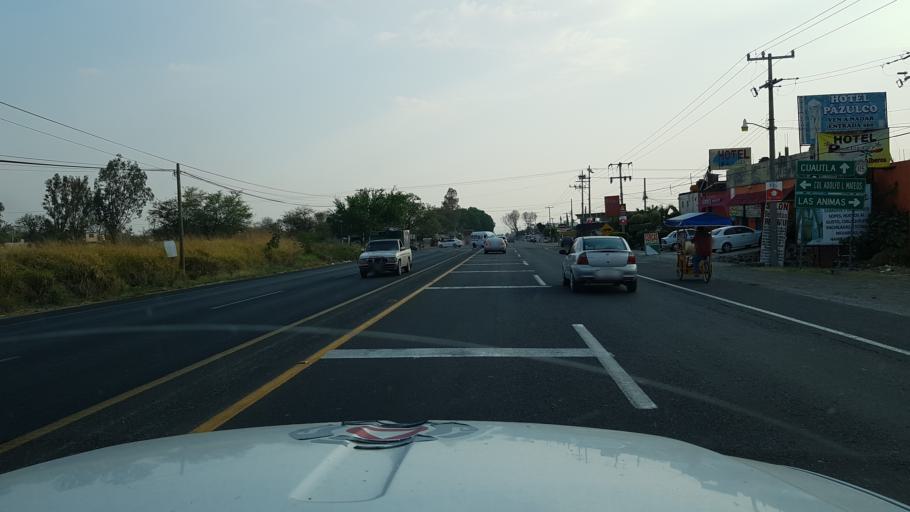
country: MX
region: Morelos
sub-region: Atlatlahucan
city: Colonia San Francisco
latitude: 18.8859
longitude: -98.9164
